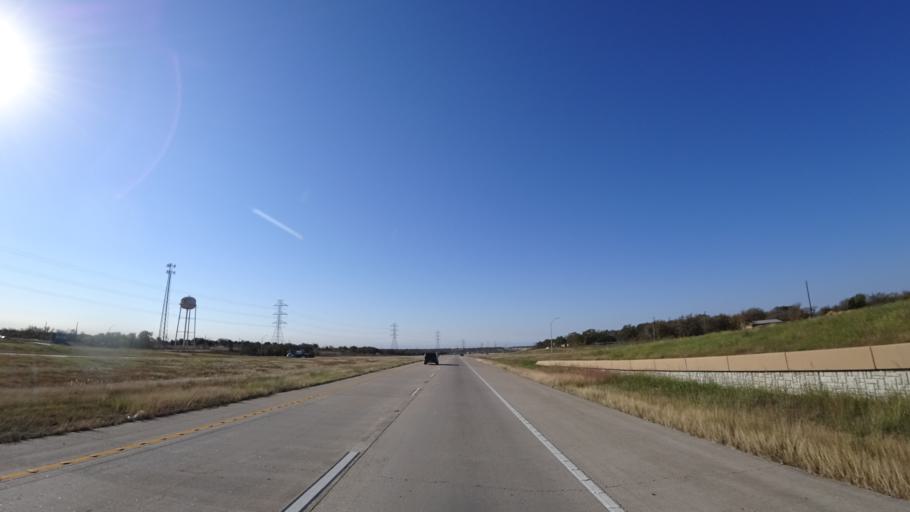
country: US
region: Texas
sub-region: Travis County
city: Hornsby Bend
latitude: 30.2864
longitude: -97.5773
